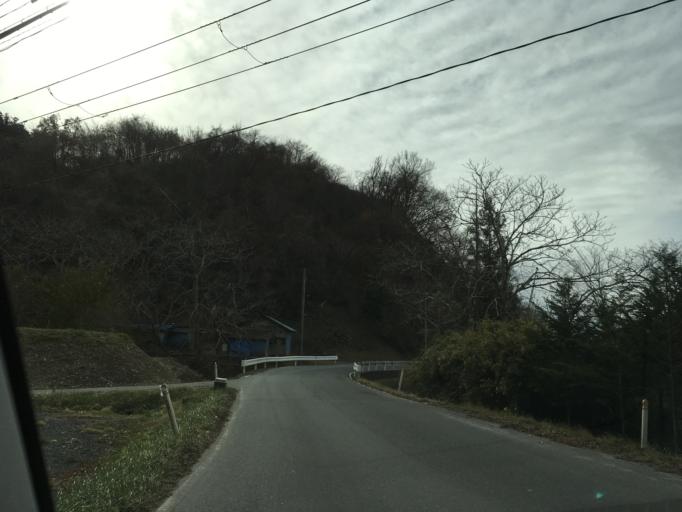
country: JP
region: Iwate
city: Ichinoseki
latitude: 38.7503
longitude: 141.2855
